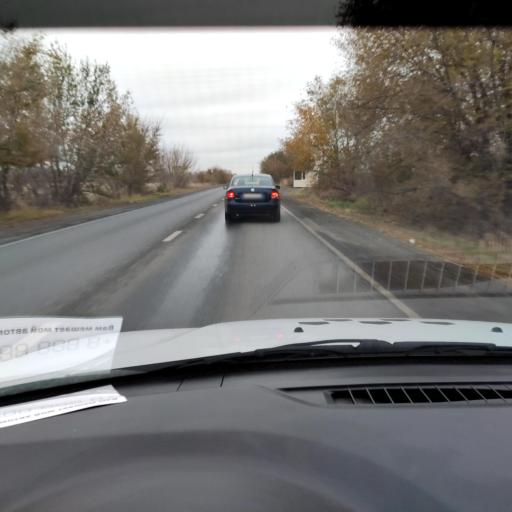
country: RU
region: Samara
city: Podstepki
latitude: 53.5181
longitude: 49.2296
